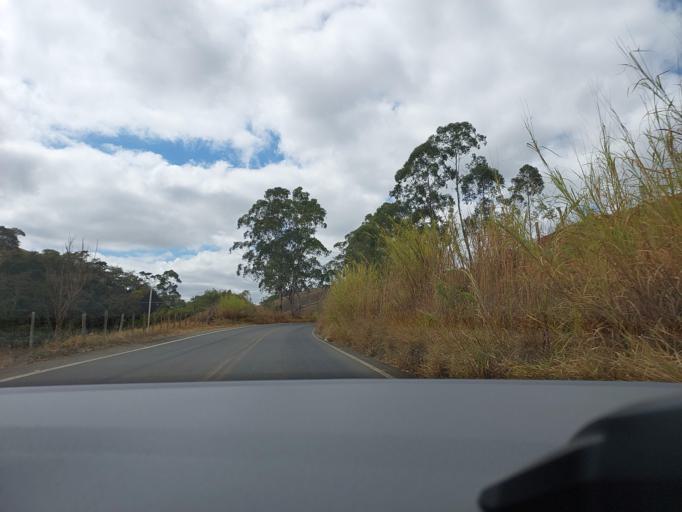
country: BR
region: Minas Gerais
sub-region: Vicosa
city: Vicosa
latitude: -20.8391
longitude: -42.7179
